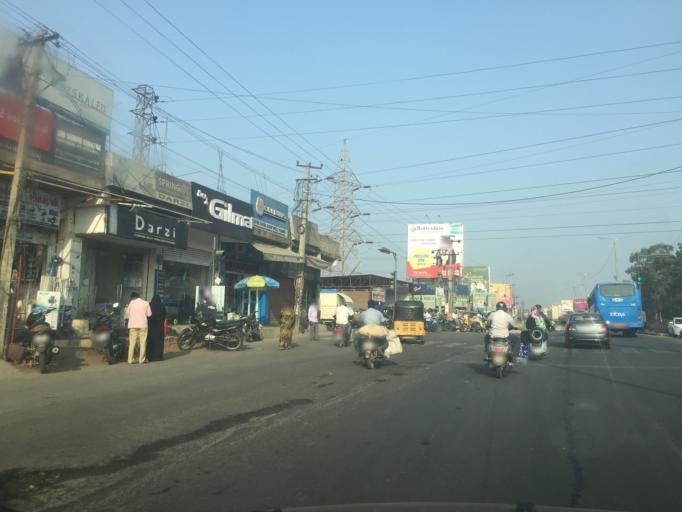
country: IN
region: Telangana
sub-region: Rangareddi
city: Uppal Kalan
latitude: 17.4047
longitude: 78.5866
